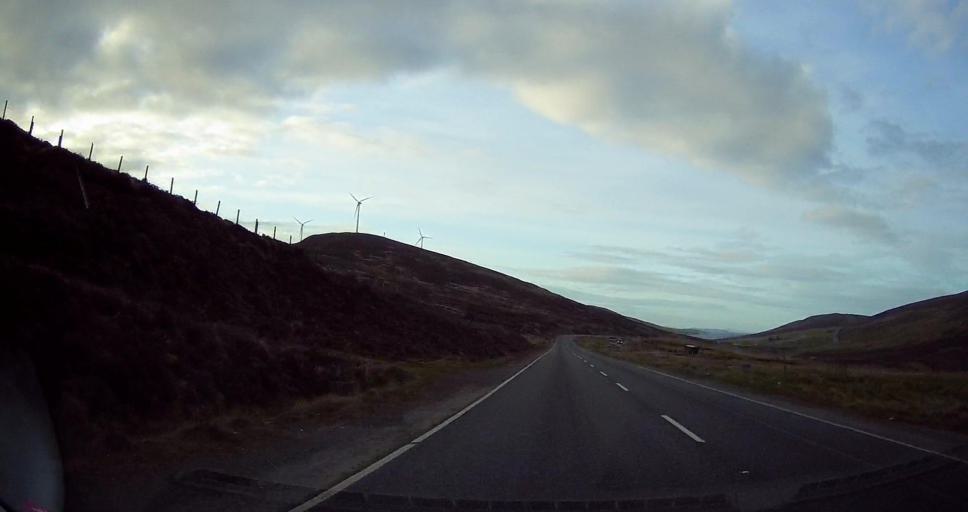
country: GB
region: Scotland
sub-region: Shetland Islands
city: Lerwick
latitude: 60.1540
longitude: -1.2352
